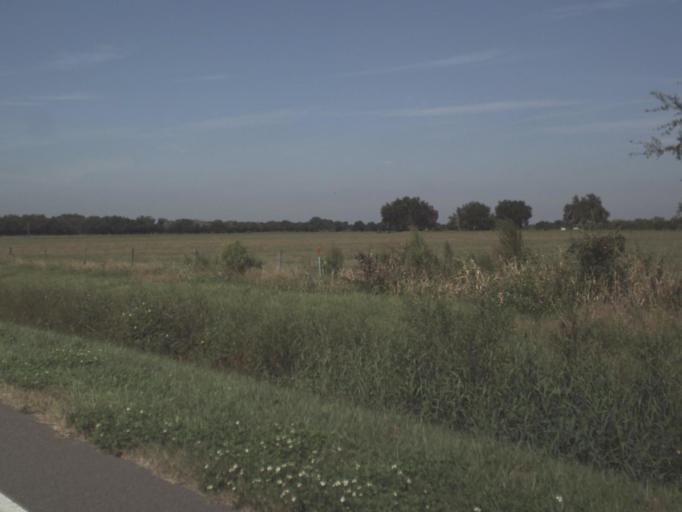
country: US
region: Florida
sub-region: Hardee County
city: Wauchula
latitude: 27.5515
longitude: -81.7370
